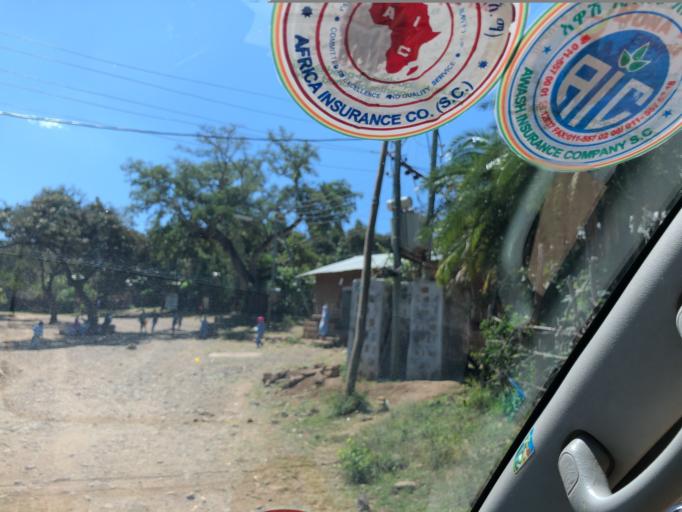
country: ET
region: Amhara
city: Werota
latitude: 11.9204
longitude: 37.7873
